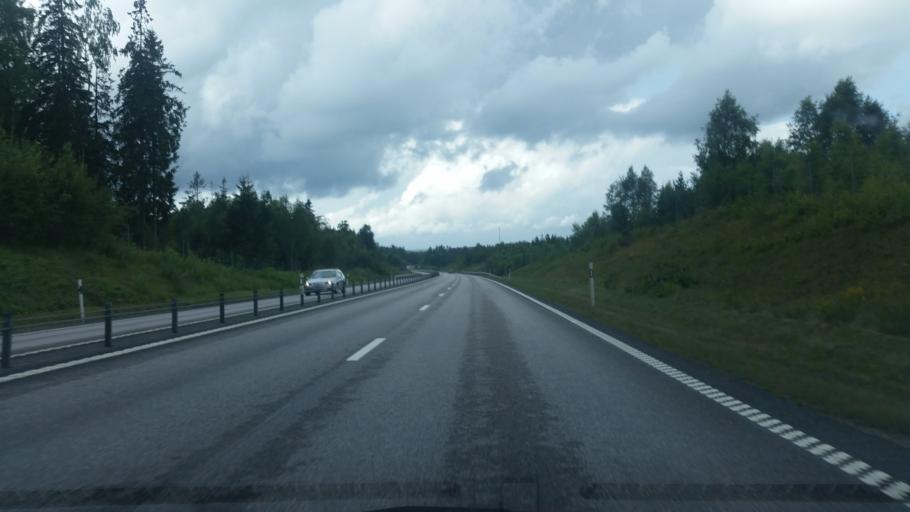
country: SE
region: Vaestra Goetaland
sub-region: Boras Kommun
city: Ganghester
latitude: 57.6530
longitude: 13.0560
